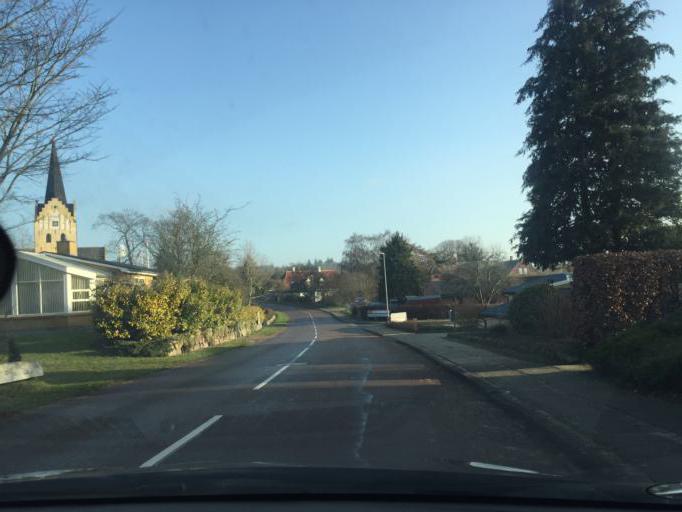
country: DK
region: South Denmark
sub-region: Faaborg-Midtfyn Kommune
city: Faaborg
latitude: 55.1267
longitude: 10.2274
